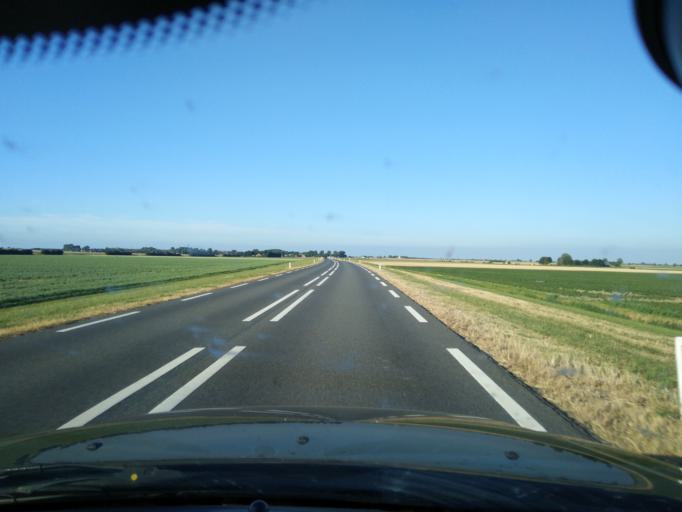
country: NL
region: Zeeland
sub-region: Schouwen-Duiveland
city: Scharendijke
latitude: 51.7137
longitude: 3.8912
